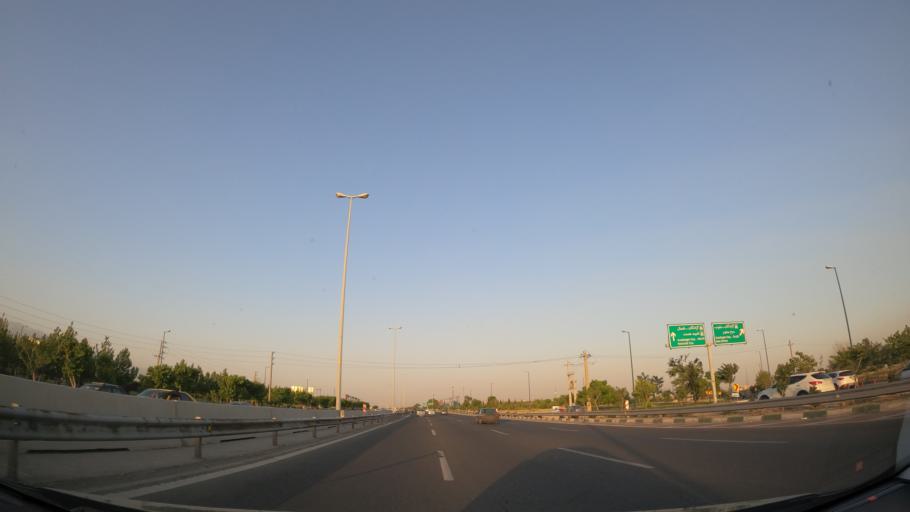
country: IR
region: Tehran
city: Shahr-e Qods
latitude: 35.7146
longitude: 51.2495
